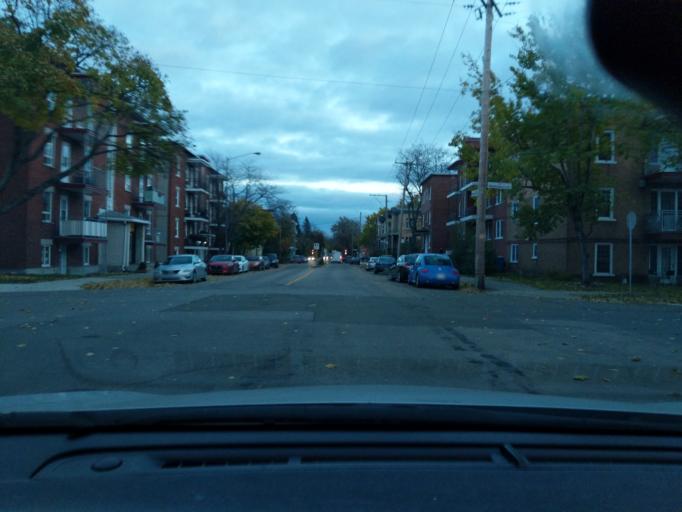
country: CA
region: Quebec
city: Quebec
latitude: 46.7919
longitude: -71.2535
